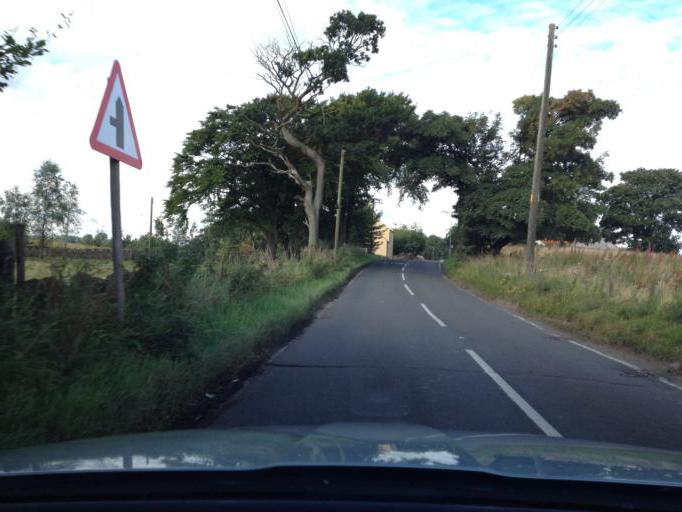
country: GB
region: Scotland
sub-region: West Lothian
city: Armadale
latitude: 55.9294
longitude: -3.7392
